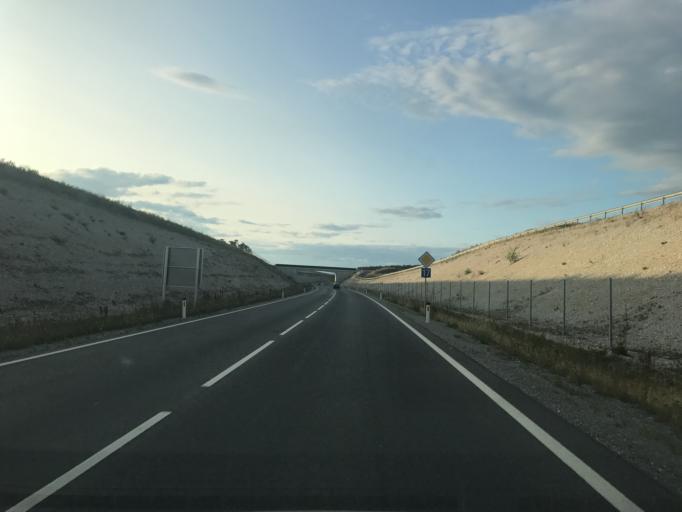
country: AT
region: Lower Austria
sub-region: Politischer Bezirk Wiener Neustadt
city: Sollenau
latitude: 47.8779
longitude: 16.2710
